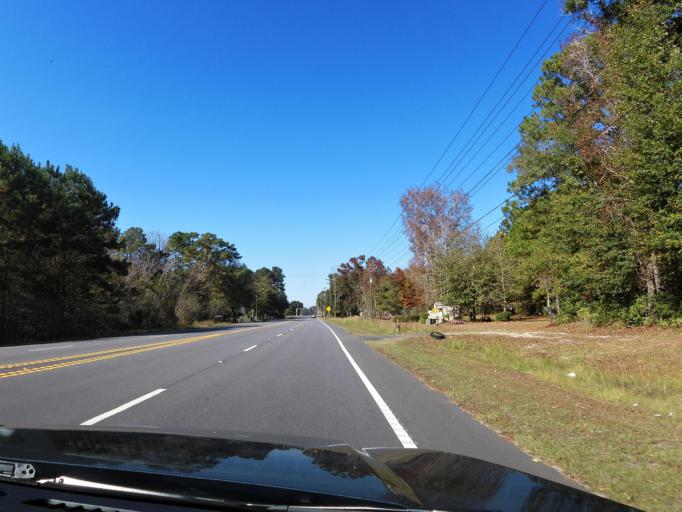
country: US
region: Georgia
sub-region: Liberty County
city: Midway
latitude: 31.7930
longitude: -81.4017
